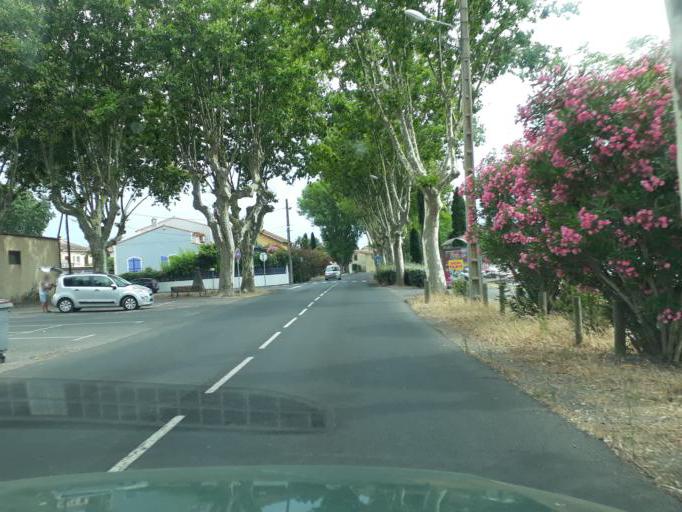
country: FR
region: Languedoc-Roussillon
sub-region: Departement de l'Herault
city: Agde
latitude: 43.3056
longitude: 3.4655
